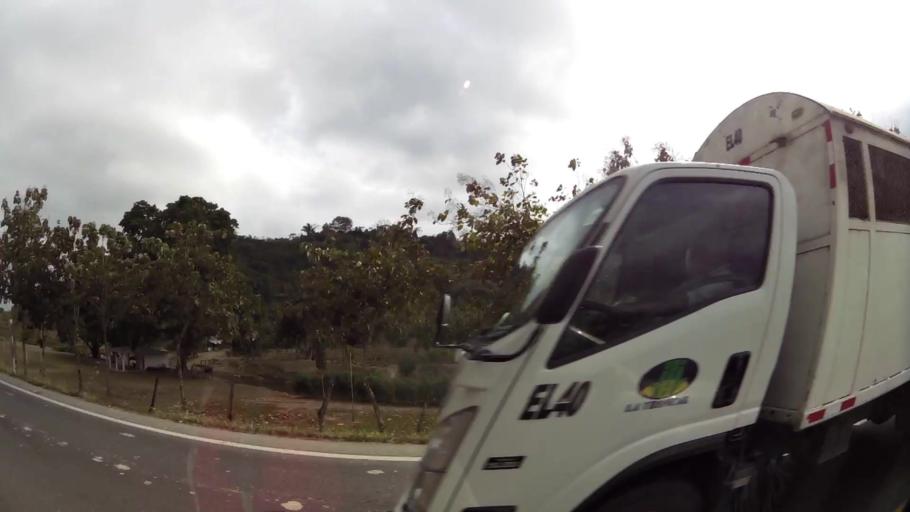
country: EC
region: Guayas
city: Naranjal
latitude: -2.4070
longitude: -79.6250
